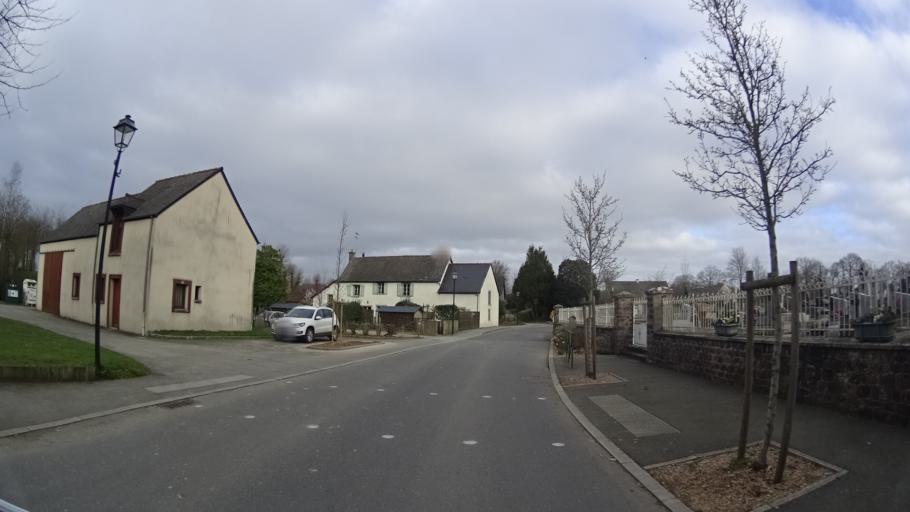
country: FR
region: Brittany
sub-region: Departement d'Ille-et-Vilaine
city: Saint-Gilles
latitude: 48.1781
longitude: -1.8529
